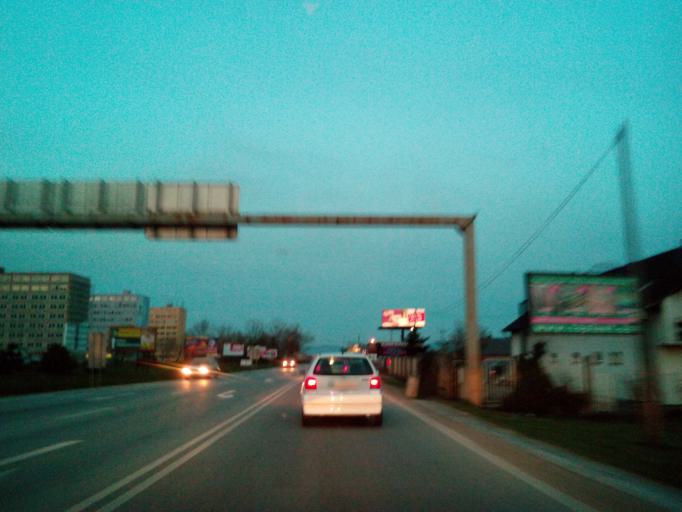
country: SK
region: Kosicky
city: Kosice
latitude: 48.6288
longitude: 21.1735
